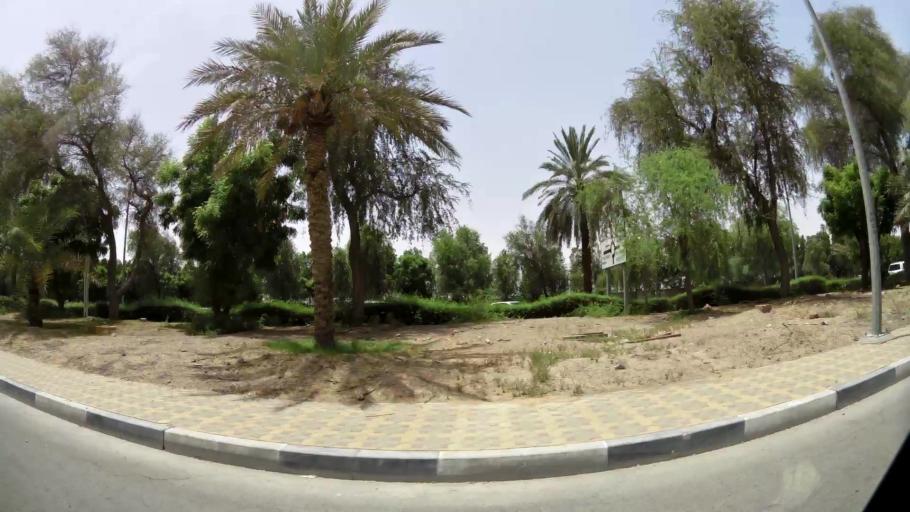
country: AE
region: Abu Dhabi
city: Al Ain
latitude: 24.2073
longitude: 55.7091
